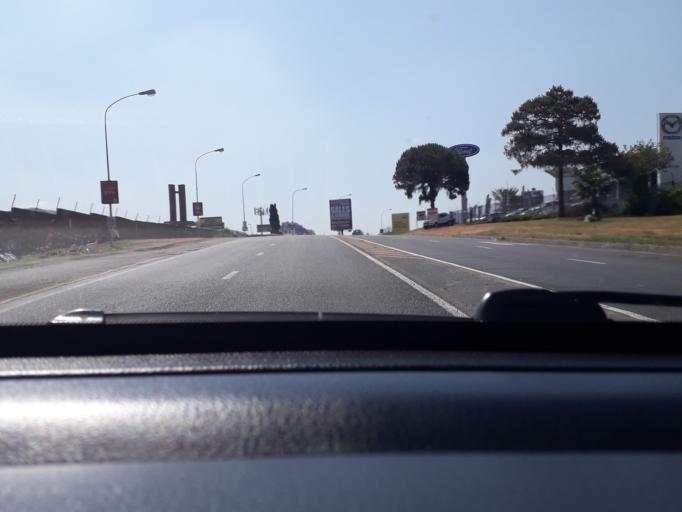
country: ZA
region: Gauteng
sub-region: City of Johannesburg Metropolitan Municipality
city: Modderfontein
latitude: -26.1243
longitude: 28.1408
